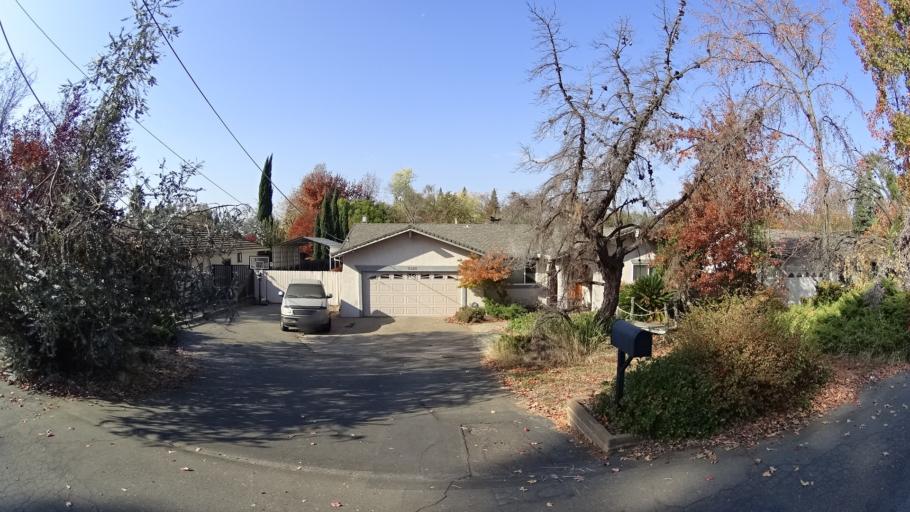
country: US
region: California
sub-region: Sacramento County
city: Citrus Heights
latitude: 38.7111
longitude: -121.2695
